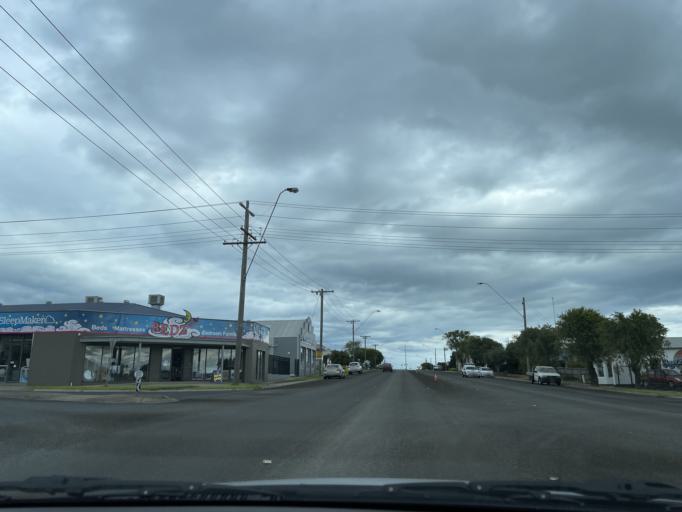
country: AU
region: Victoria
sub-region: Glenelg
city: Portland
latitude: -38.3378
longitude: 141.6042
